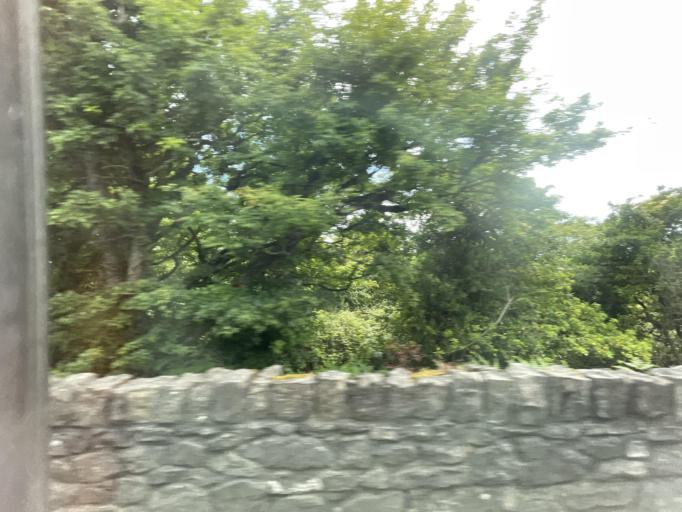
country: GB
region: Wales
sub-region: Anglesey
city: Llanfachraeth
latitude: 53.2602
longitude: -4.4319
